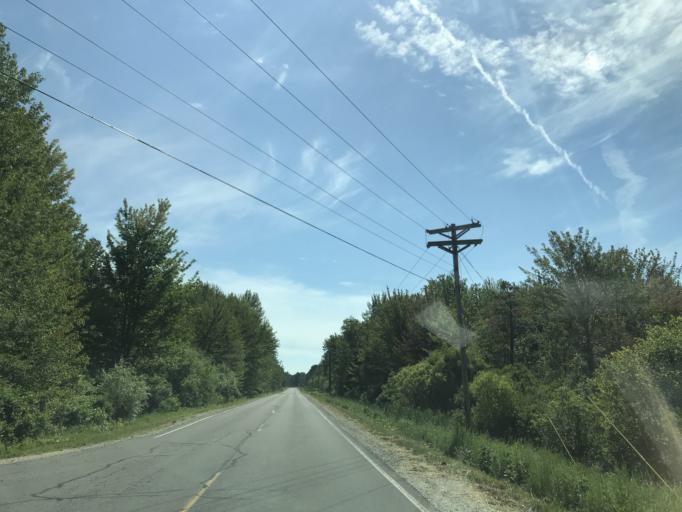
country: US
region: Michigan
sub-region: Grand Traverse County
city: Traverse City
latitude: 44.6583
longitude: -85.7273
